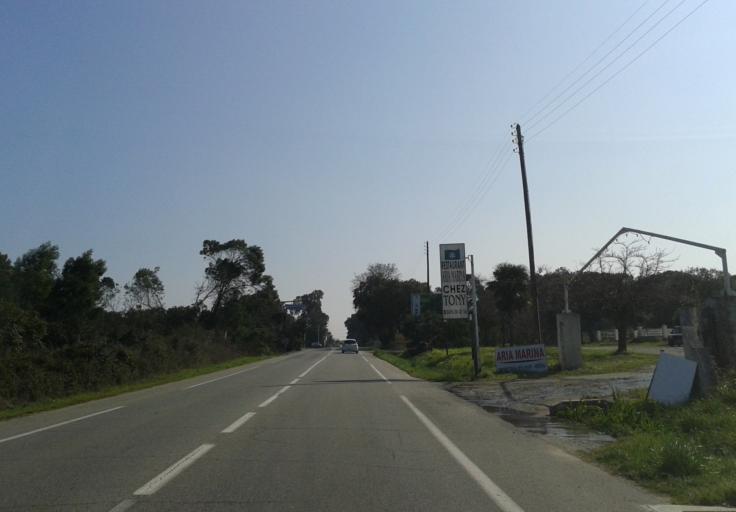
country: FR
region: Corsica
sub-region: Departement de la Haute-Corse
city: San-Nicolao
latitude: 42.3423
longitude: 9.5345
